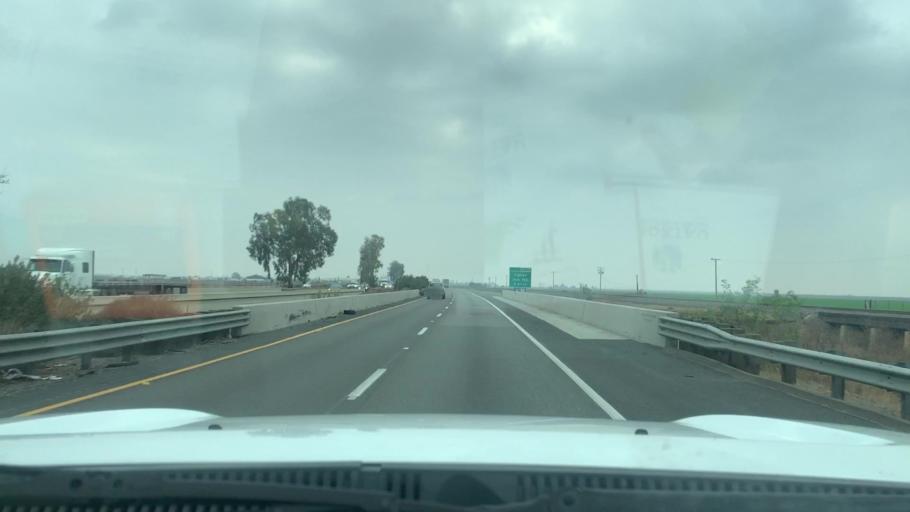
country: US
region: California
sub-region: Tulare County
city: Tipton
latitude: 36.0945
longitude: -119.3223
